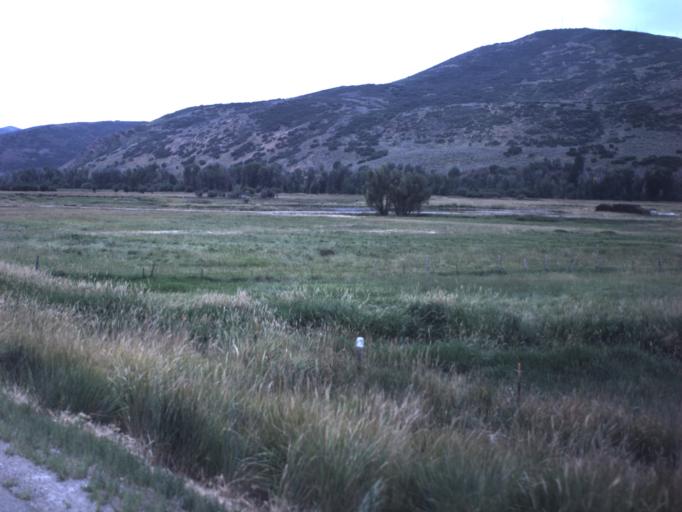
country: US
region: Utah
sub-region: Summit County
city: Oakley
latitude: 40.7349
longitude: -111.3494
